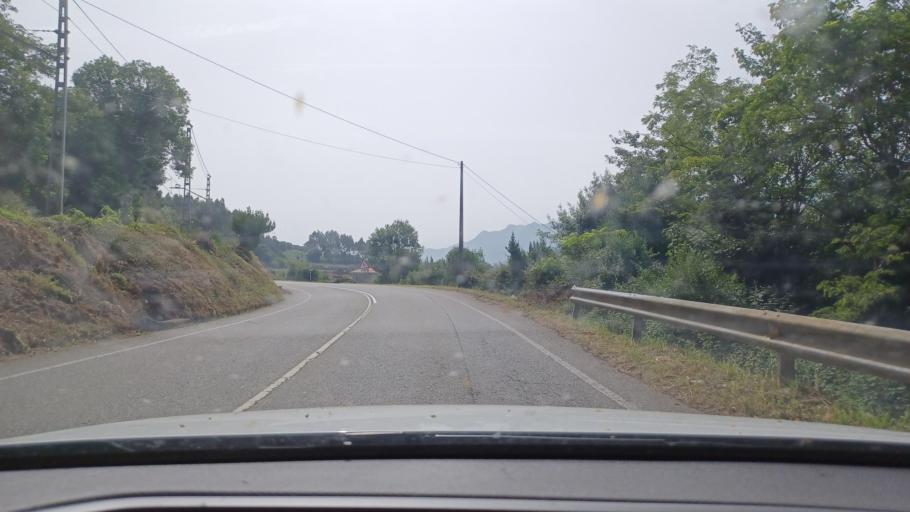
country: ES
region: Asturias
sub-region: Province of Asturias
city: Ribadesella
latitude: 43.4597
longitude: -5.0495
